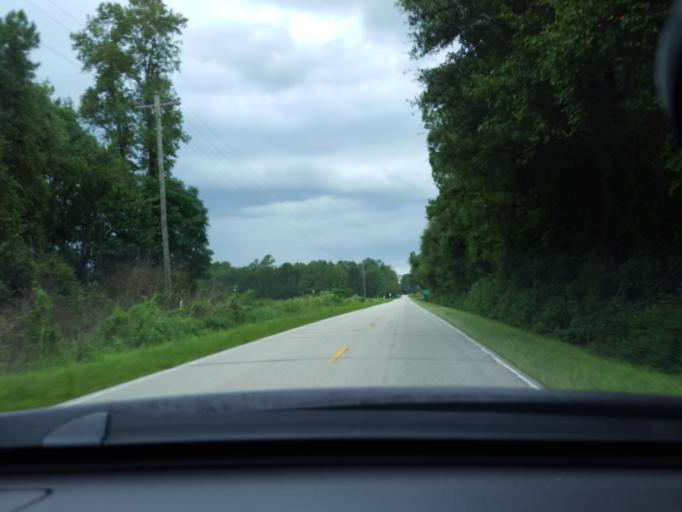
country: US
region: North Carolina
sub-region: Duplin County
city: Rose Hill
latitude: 34.8006
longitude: -78.2336
